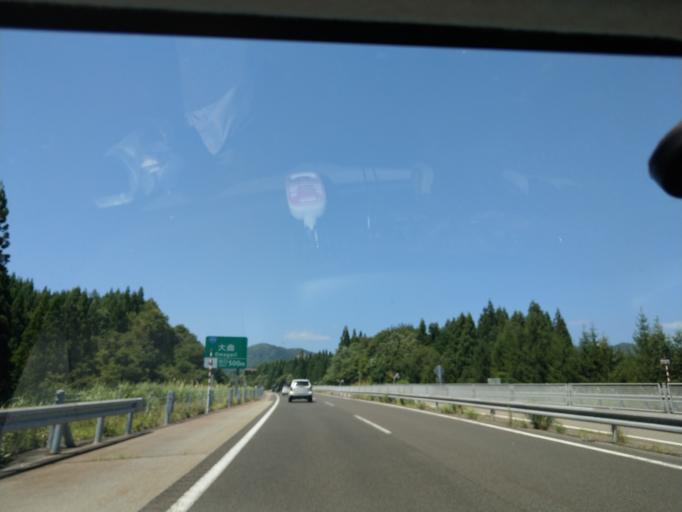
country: JP
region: Akita
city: Omagari
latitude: 39.4230
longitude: 140.4324
